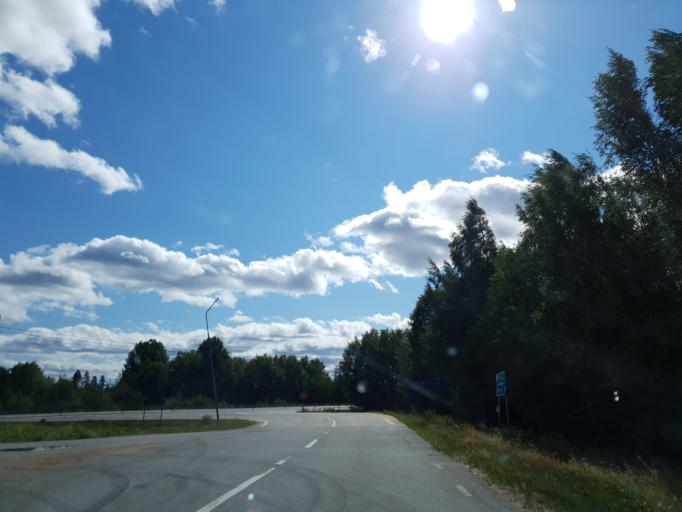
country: SE
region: Vaesterbotten
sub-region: Nordmalings Kommun
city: Nordmaling
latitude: 63.5353
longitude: 19.3993
